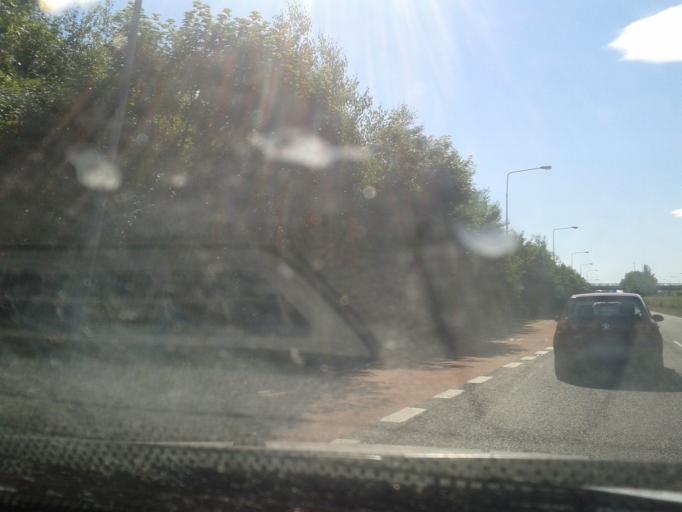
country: IE
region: Leinster
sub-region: Fingal County
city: Blanchardstown
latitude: 53.3935
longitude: -6.3841
